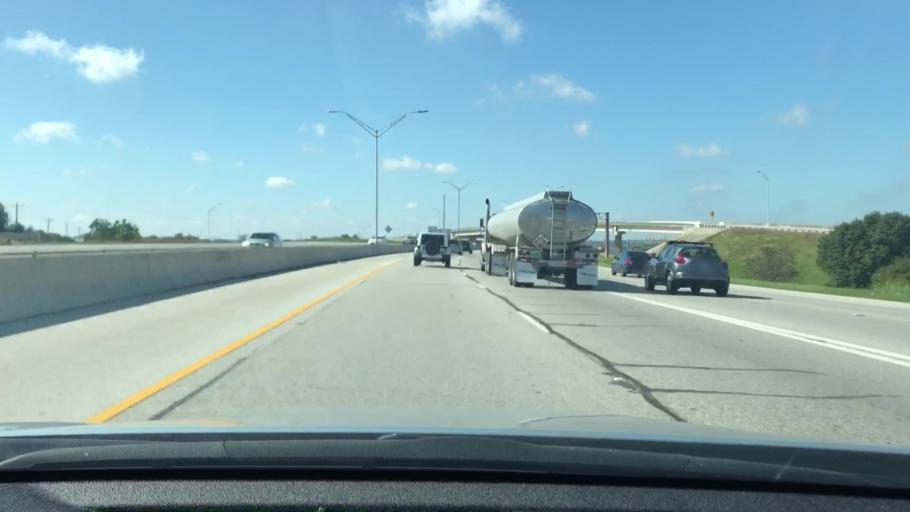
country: US
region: Texas
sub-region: Bexar County
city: Windcrest
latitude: 29.5177
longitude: -98.4006
